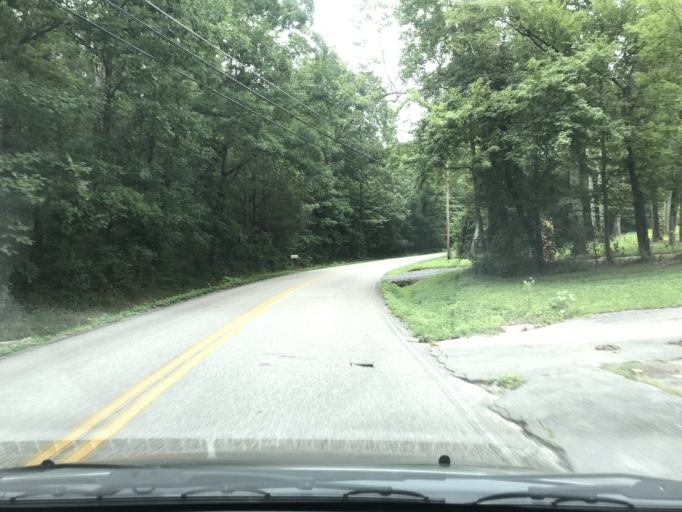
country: US
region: Tennessee
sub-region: Hamilton County
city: Lakesite
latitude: 35.1704
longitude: -85.0793
